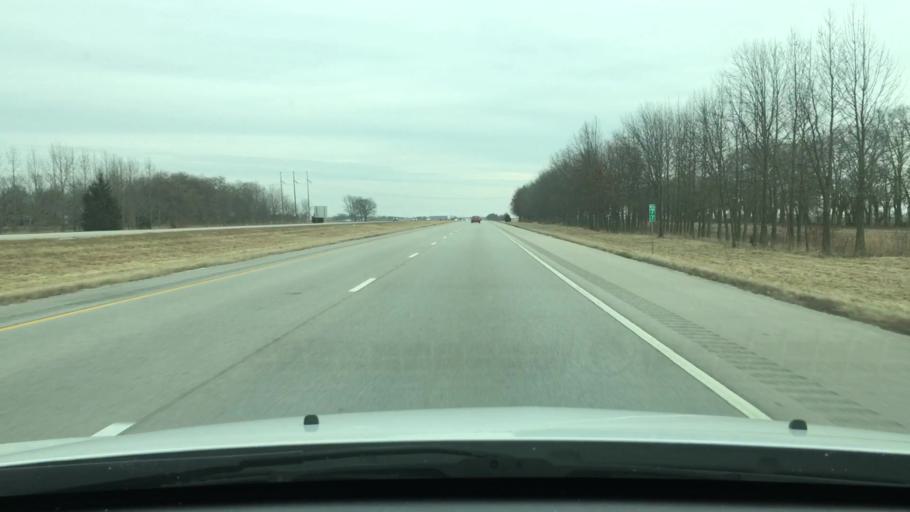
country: US
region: Illinois
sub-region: Sangamon County
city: New Berlin
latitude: 39.7368
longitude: -90.0191
